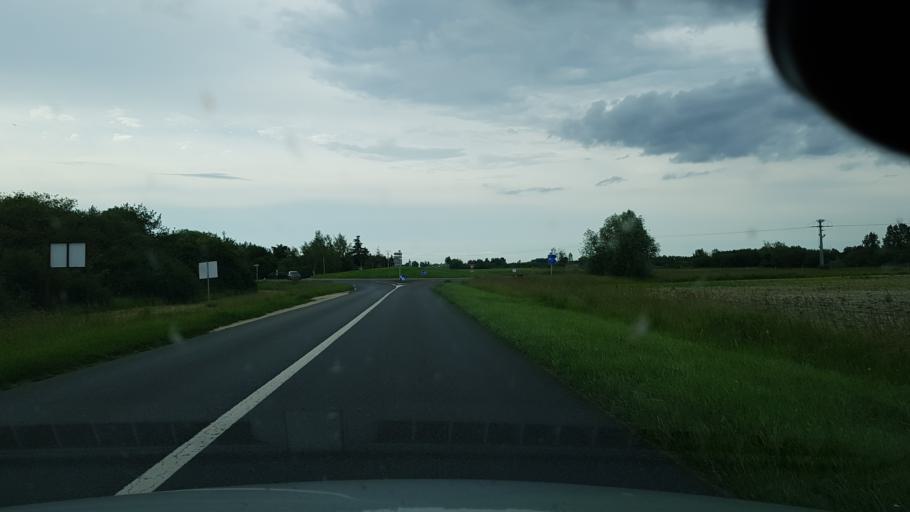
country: FR
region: Centre
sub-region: Departement du Loir-et-Cher
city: Chatillon-sur-Cher
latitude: 47.3196
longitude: 1.4972
